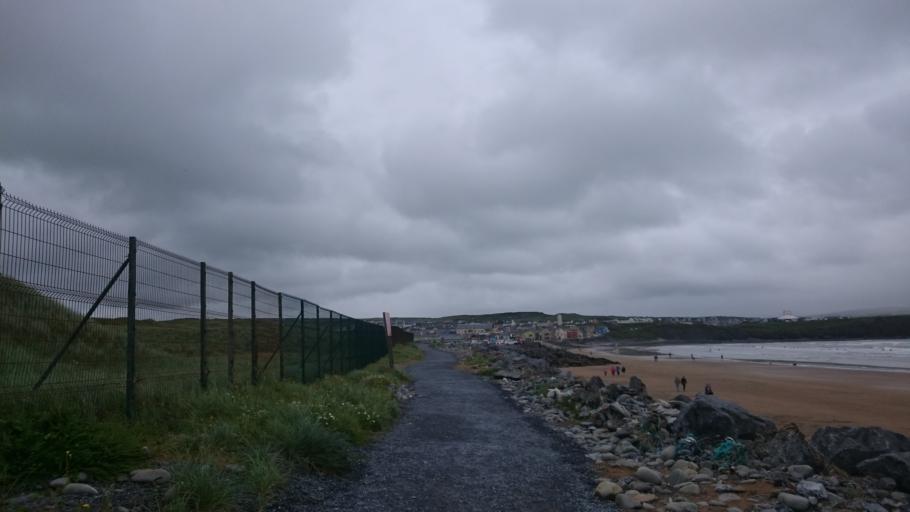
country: IE
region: Munster
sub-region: An Clar
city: Kilrush
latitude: 52.9367
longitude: -9.3526
